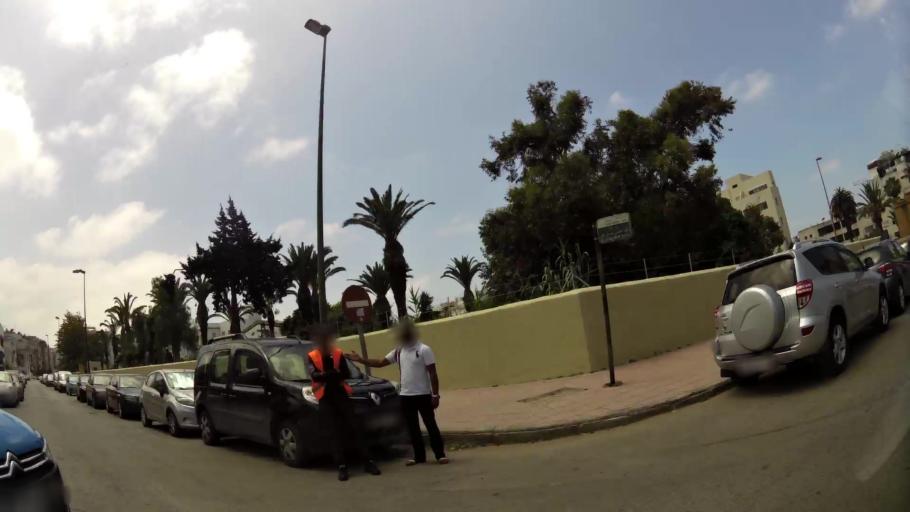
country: MA
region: Rabat-Sale-Zemmour-Zaer
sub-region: Rabat
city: Rabat
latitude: 34.0066
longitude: -6.8478
